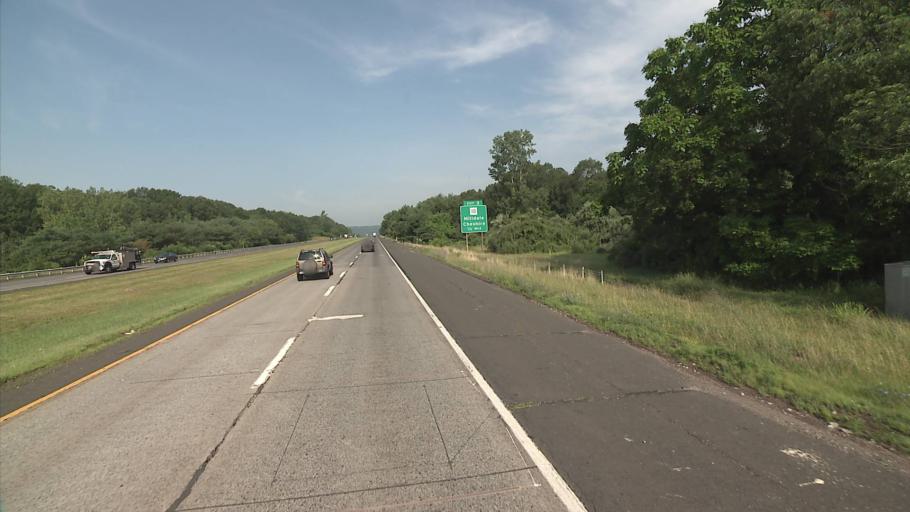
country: US
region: Connecticut
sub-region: New Haven County
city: Cheshire Village
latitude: 41.5558
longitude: -72.8748
